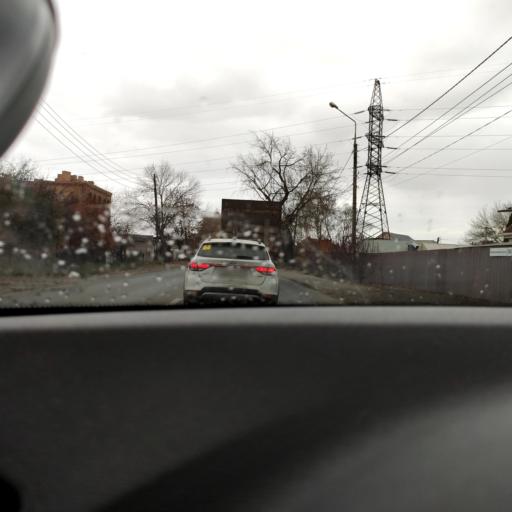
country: RU
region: Samara
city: Smyshlyayevka
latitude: 53.2367
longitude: 50.3184
